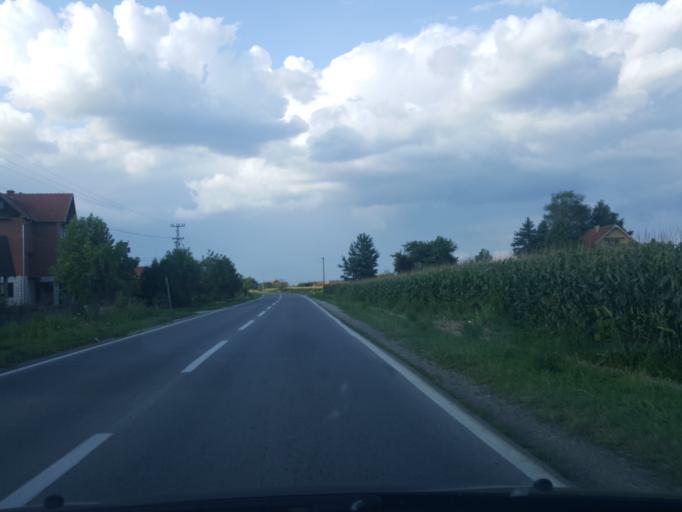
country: RS
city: Kozjak
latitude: 44.6267
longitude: 19.2713
